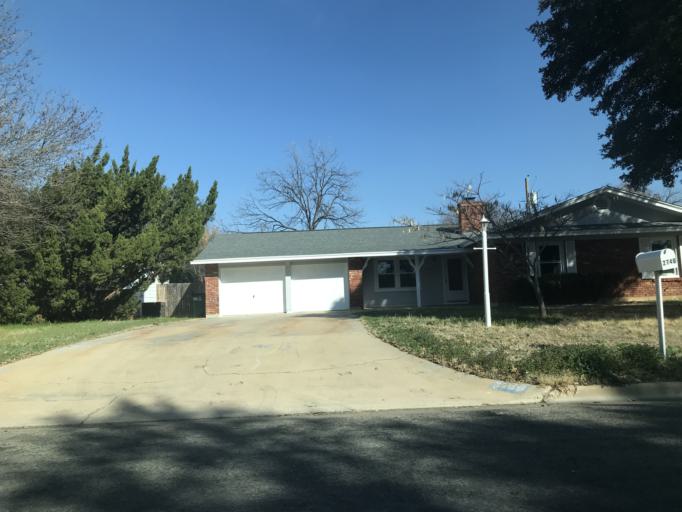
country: US
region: Texas
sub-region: Tom Green County
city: San Angelo
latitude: 31.4350
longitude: -100.4725
